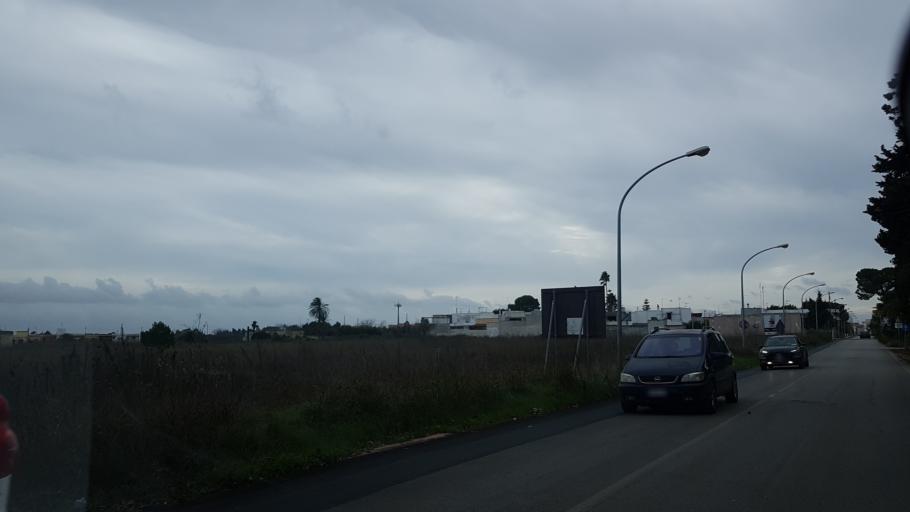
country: IT
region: Apulia
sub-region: Provincia di Brindisi
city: Mesagne
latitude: 40.5682
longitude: 17.7997
